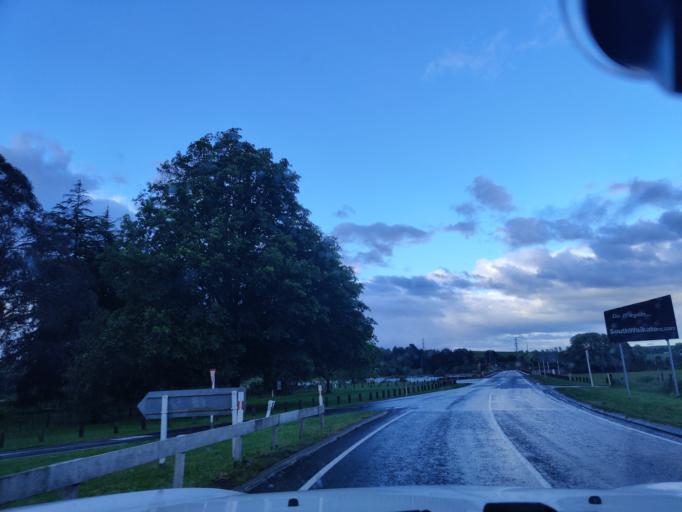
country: NZ
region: Waikato
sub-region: South Waikato District
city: Tokoroa
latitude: -38.4186
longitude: 175.8108
